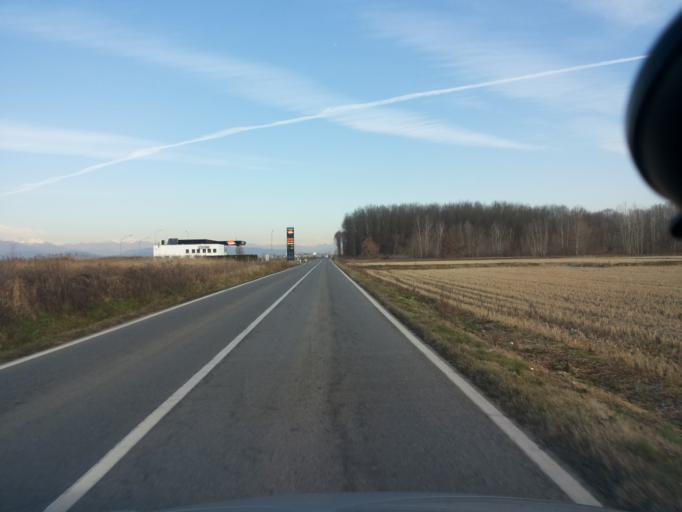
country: IT
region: Piedmont
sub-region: Provincia di Vercelli
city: Greggio
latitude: 45.4675
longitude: 8.3866
